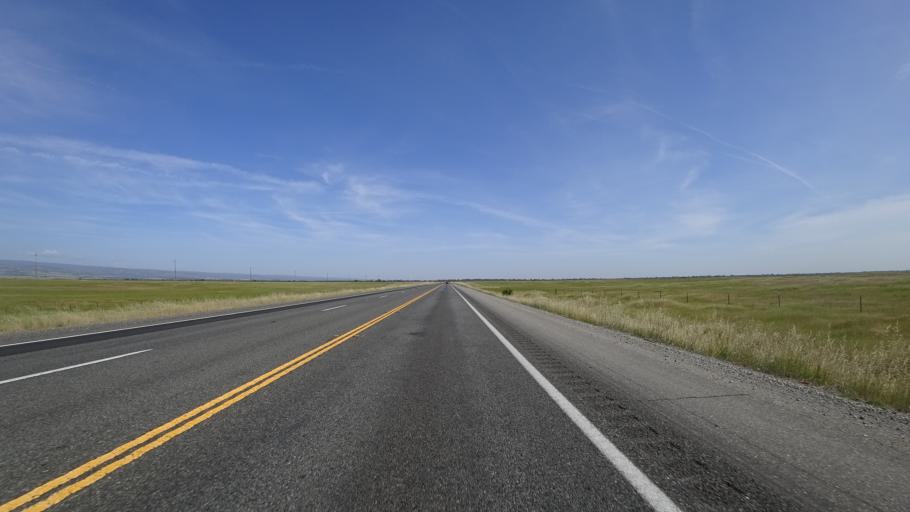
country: US
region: California
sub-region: Tehama County
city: Los Molinos
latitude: 39.9060
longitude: -122.0035
